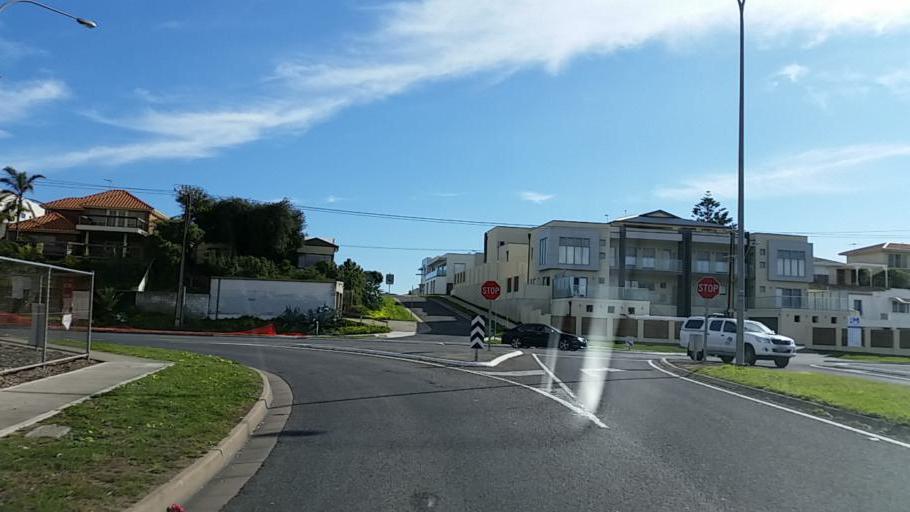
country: AU
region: South Australia
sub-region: Charles Sturt
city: Grange
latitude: -34.8945
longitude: 138.4892
